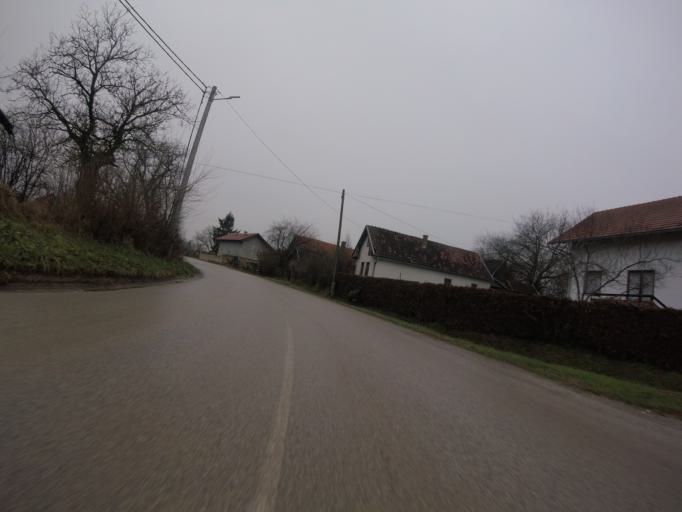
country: HR
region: Sisacko-Moslavacka
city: Lekenik
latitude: 45.6560
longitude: 16.2610
